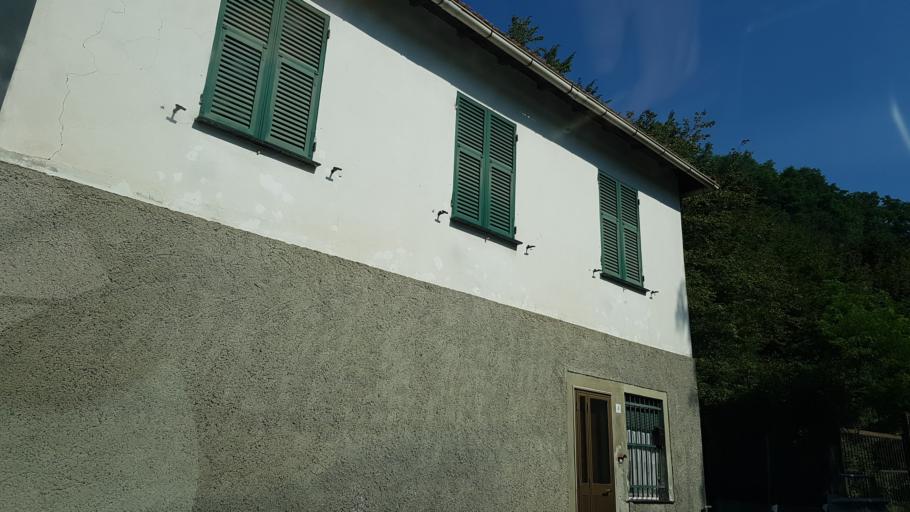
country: IT
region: Liguria
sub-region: Provincia di Genova
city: Serra Ricco
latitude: 44.5189
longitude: 8.9392
